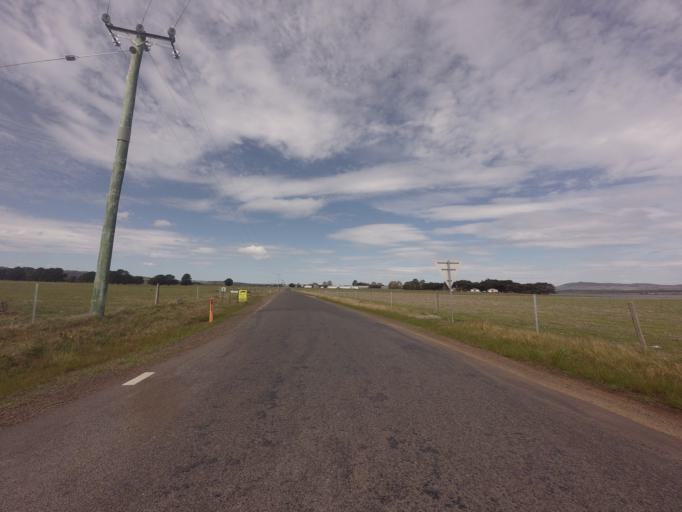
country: AU
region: Tasmania
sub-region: Northern Midlands
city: Evandale
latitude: -41.8091
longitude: 147.2831
